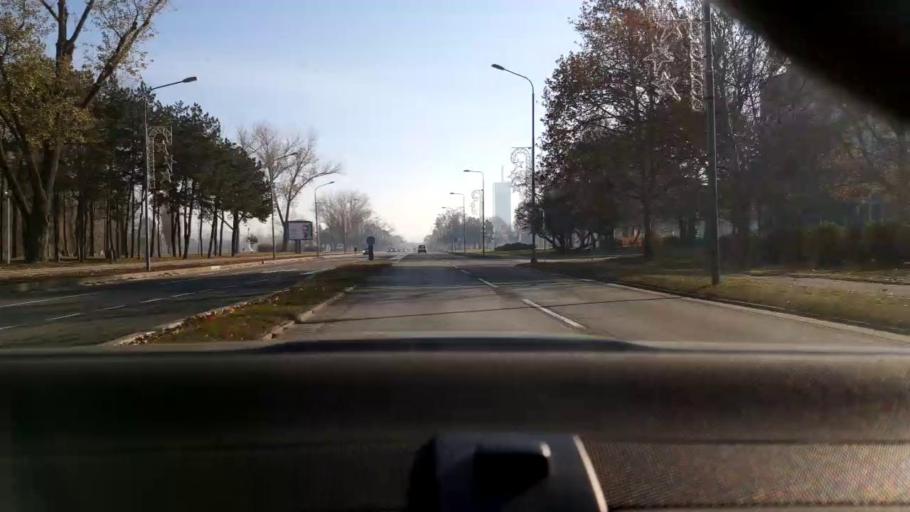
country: RS
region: Central Serbia
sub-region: Belgrade
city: Novi Beograd
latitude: 44.8227
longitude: 20.4260
